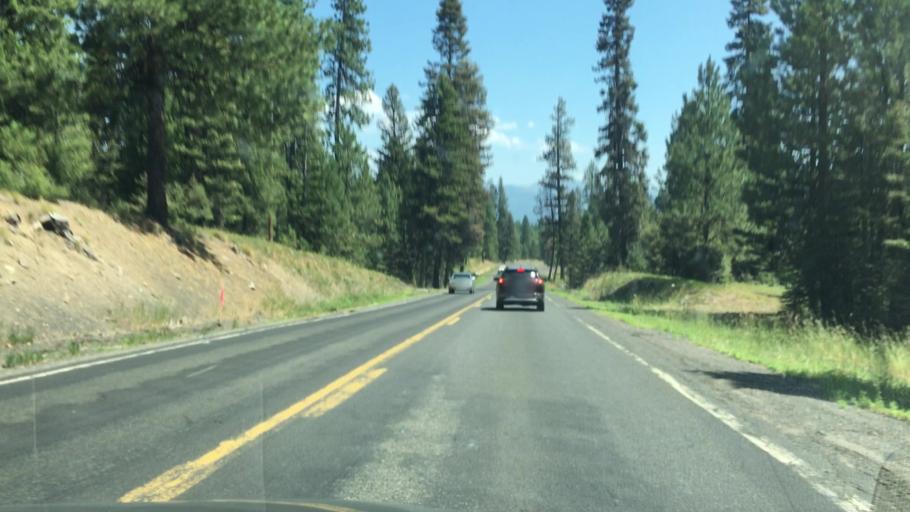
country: US
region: Idaho
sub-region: Valley County
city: McCall
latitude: 44.9278
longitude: -116.1486
